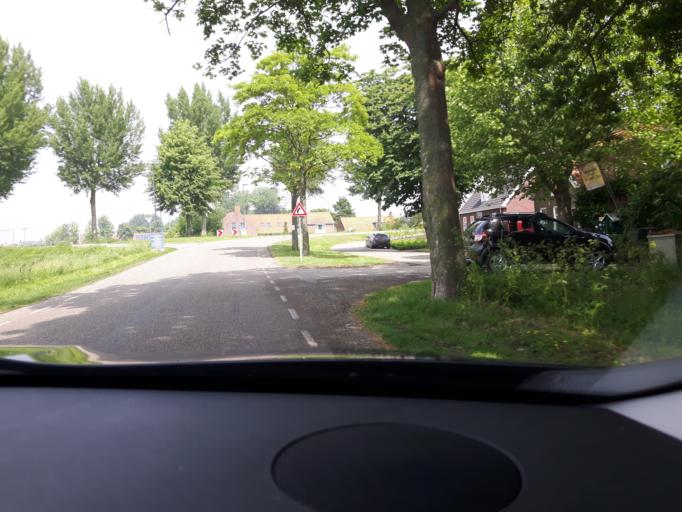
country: NL
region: Zeeland
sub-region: Gemeente Goes
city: Goes
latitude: 51.4307
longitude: 3.8780
